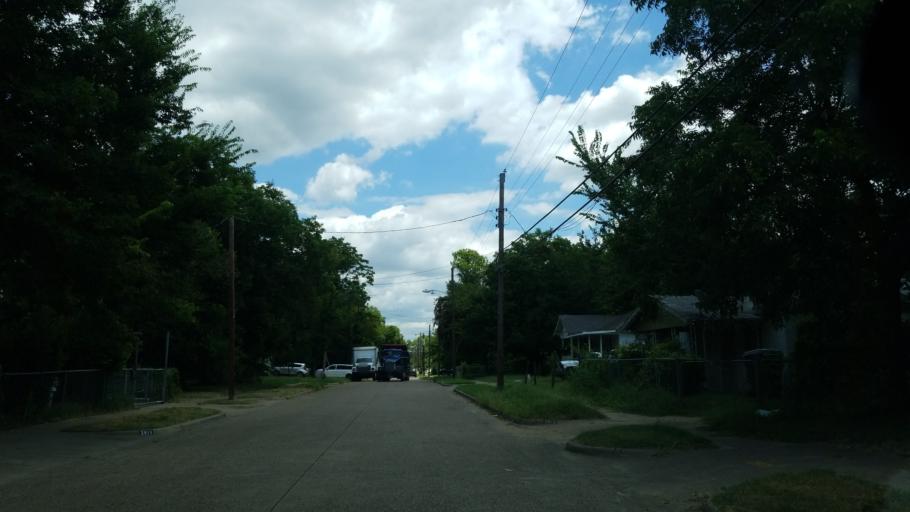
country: US
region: Texas
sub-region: Dallas County
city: Dallas
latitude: 32.7427
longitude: -96.7502
